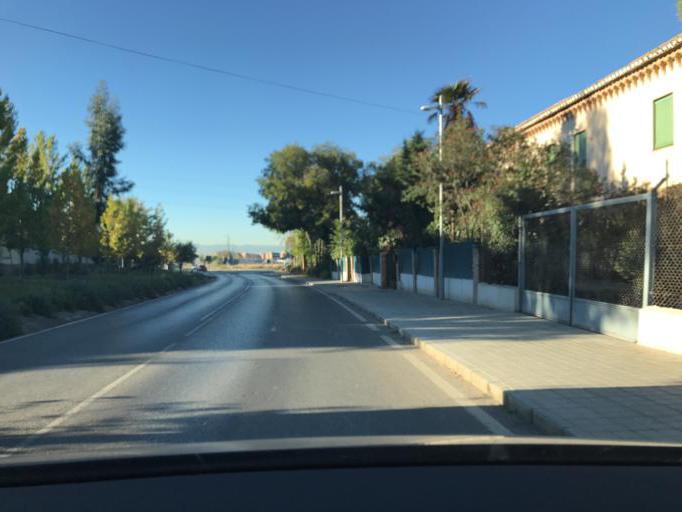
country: ES
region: Andalusia
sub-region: Provincia de Granada
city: Jun
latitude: 37.2140
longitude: -3.5922
